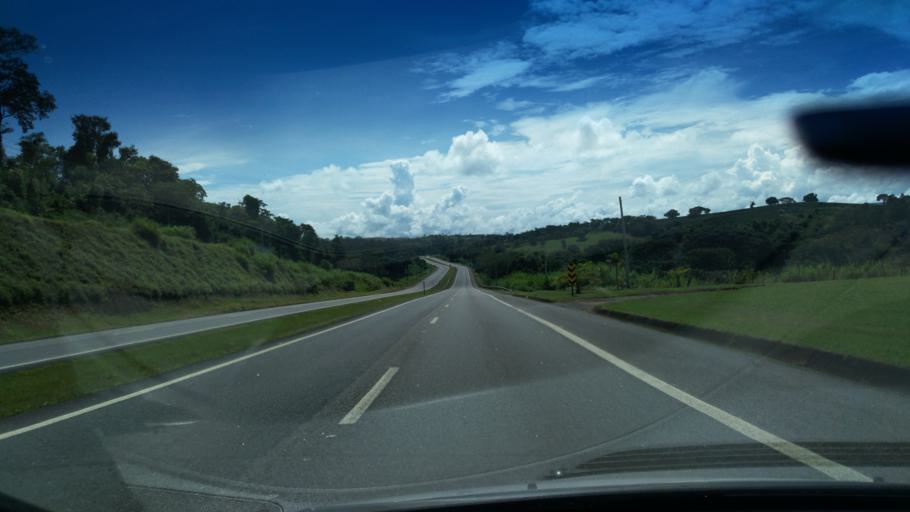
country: BR
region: Sao Paulo
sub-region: Santo Antonio Do Jardim
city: Espirito Santo do Pinhal
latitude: -22.2350
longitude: -46.7979
